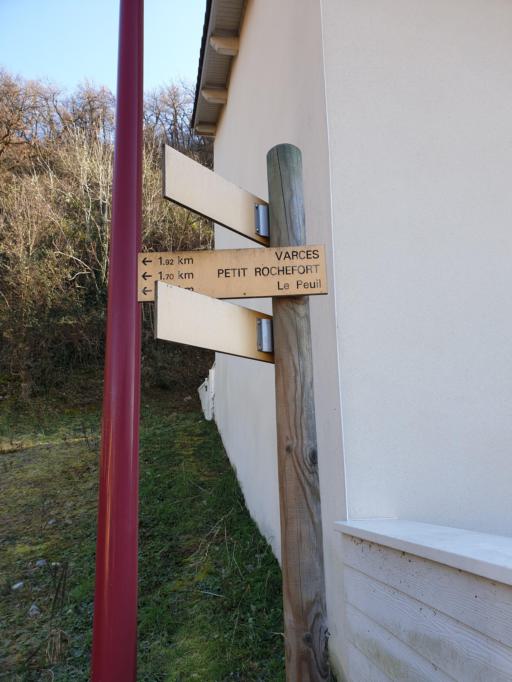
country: FR
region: Rhone-Alpes
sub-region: Departement de l'Isere
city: Allieres-et-Risset
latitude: 45.1019
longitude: 5.6898
